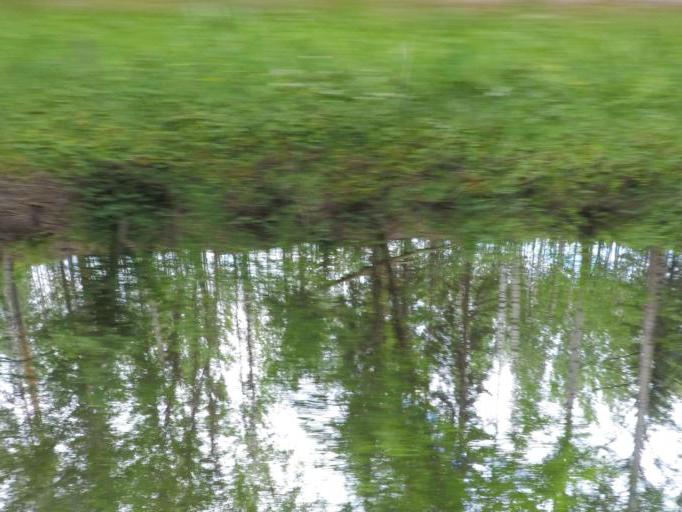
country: FI
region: Uusimaa
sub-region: Porvoo
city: Pukkila
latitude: 60.8067
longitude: 25.4796
